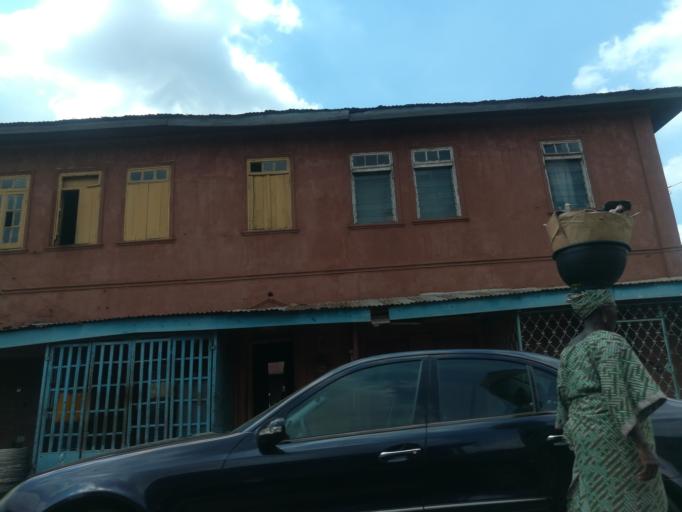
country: NG
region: Oyo
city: Ibadan
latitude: 7.3936
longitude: 3.8870
